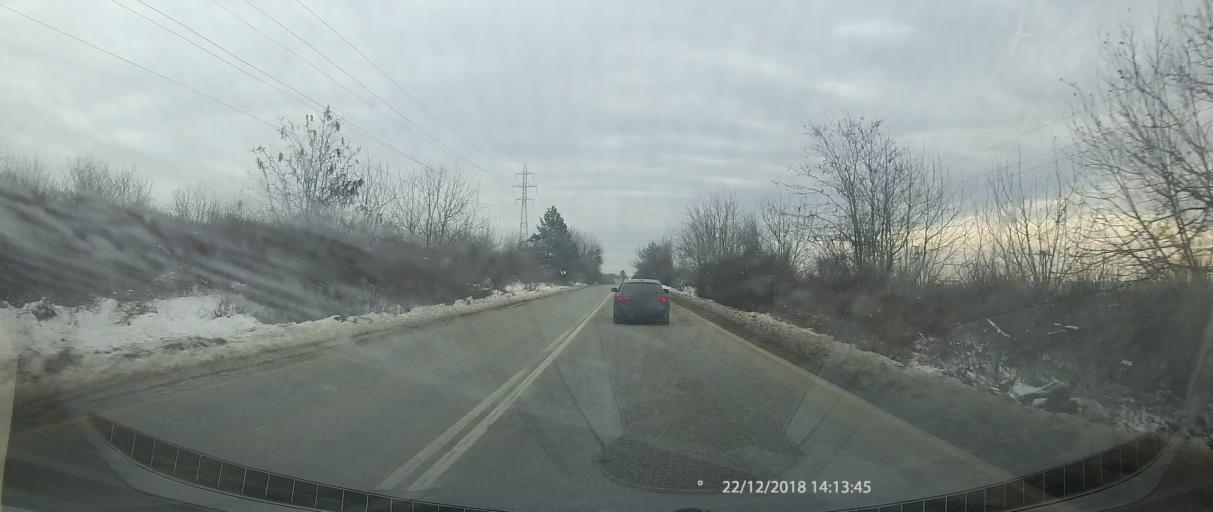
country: BG
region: Pleven
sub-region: Obshtina Pleven
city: Pleven
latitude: 43.4342
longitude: 24.6083
